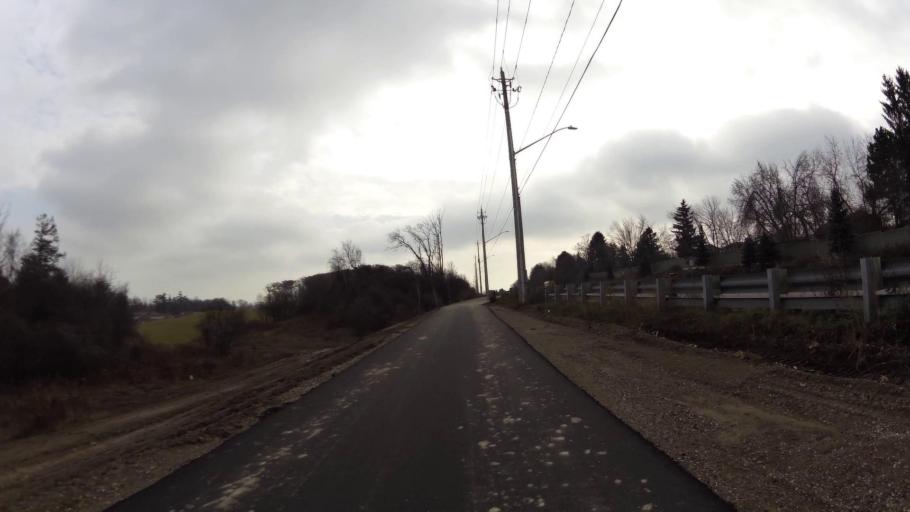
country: CA
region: Ontario
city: Kitchener
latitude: 43.4151
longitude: -80.4665
